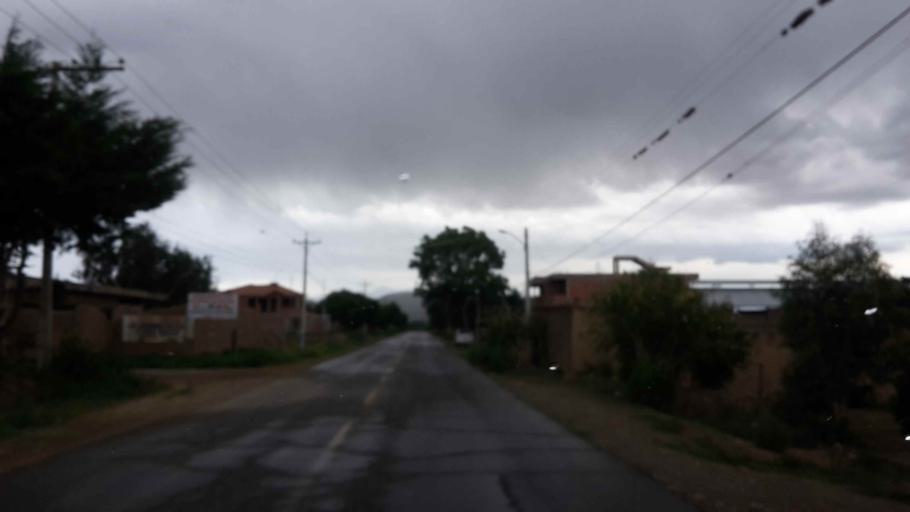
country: BO
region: Cochabamba
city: Tarata
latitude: -17.5769
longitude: -66.0603
